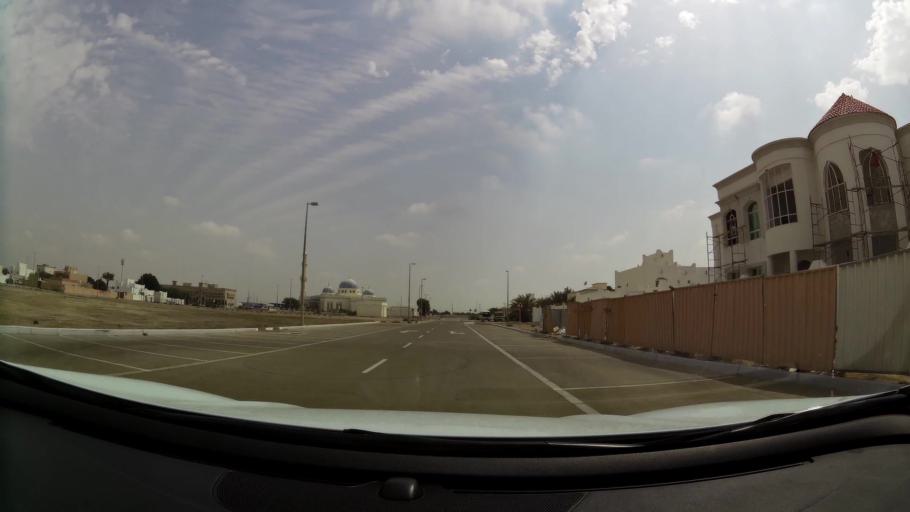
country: AE
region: Abu Dhabi
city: Abu Dhabi
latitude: 24.5416
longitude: 54.6322
